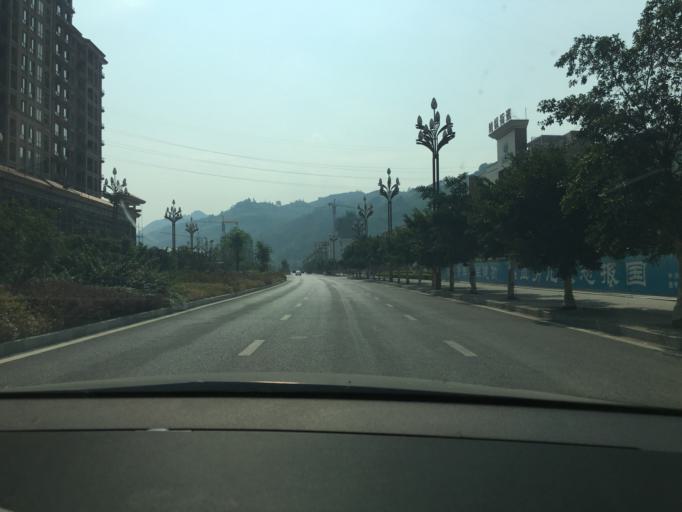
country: CN
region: Guangxi Zhuangzu Zizhiqu
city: Xinzhou
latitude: 24.9947
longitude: 105.7843
